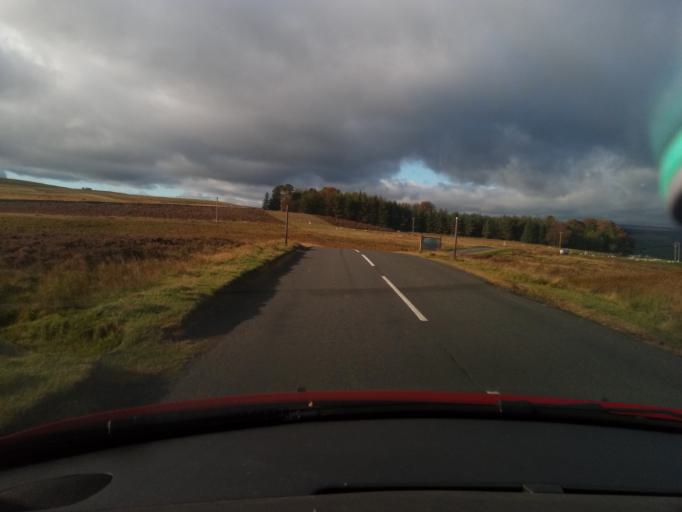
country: GB
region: Scotland
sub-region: The Scottish Borders
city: Lauder
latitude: 55.7008
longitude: -2.8221
